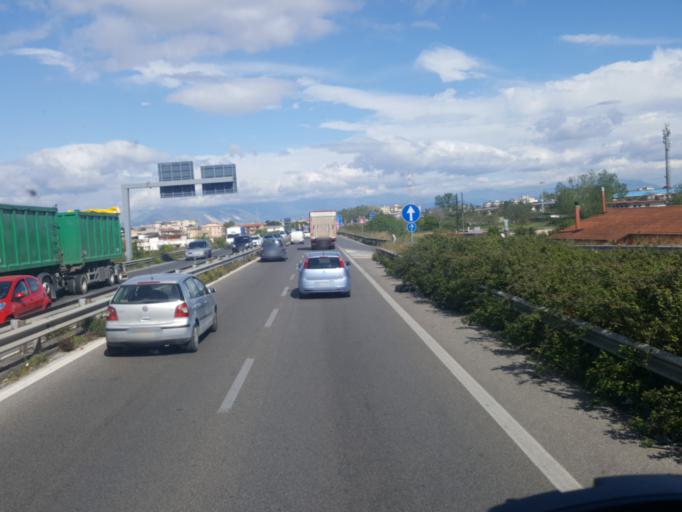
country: IT
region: Campania
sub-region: Provincia di Napoli
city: Sant'Antimo
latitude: 40.9336
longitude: 14.2238
